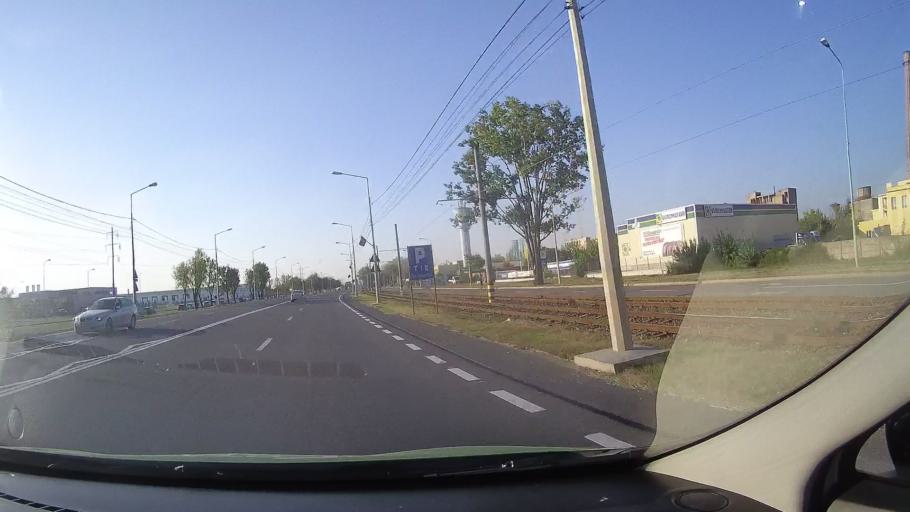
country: RO
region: Bihor
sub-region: Comuna Santandrei
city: Santandrei
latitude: 47.0850
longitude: 21.8836
